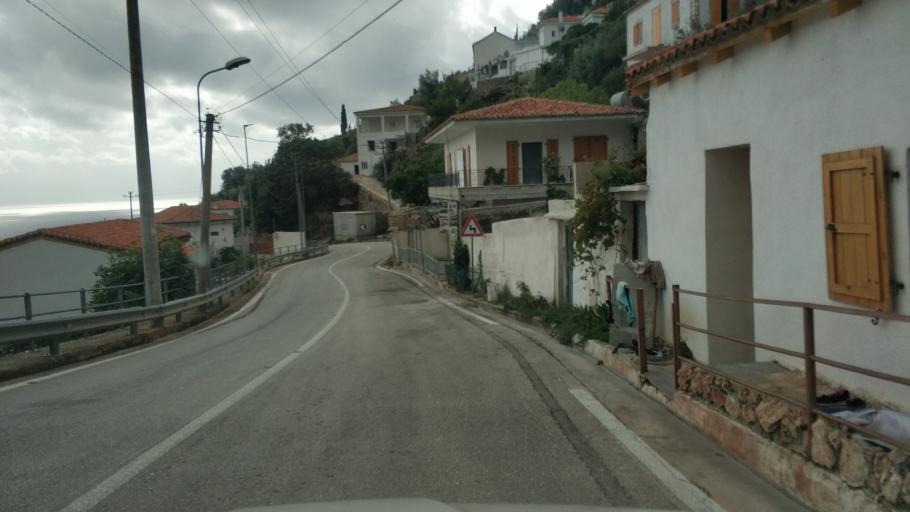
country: AL
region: Vlore
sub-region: Rrethi i Vlores
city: Vranisht
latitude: 40.1542
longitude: 19.6376
